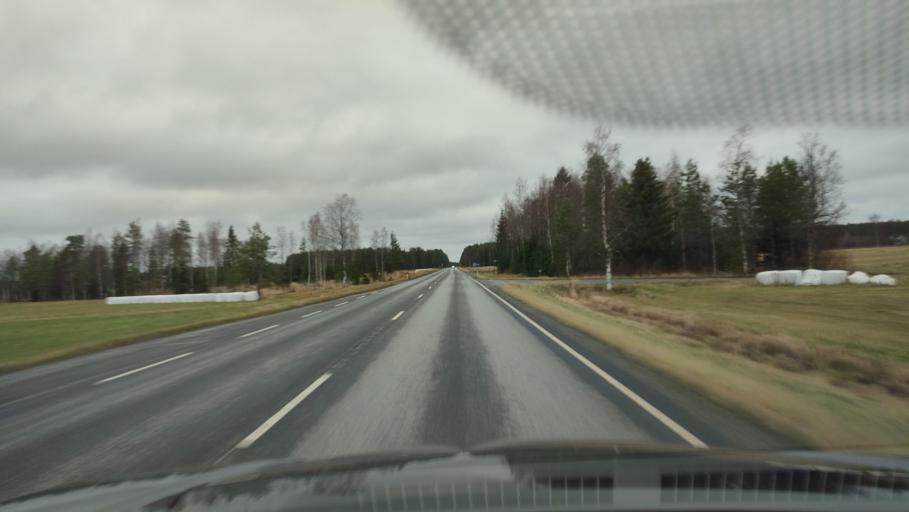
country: FI
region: Southern Ostrobothnia
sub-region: Suupohja
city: Kauhajoki
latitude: 62.5016
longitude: 22.3027
